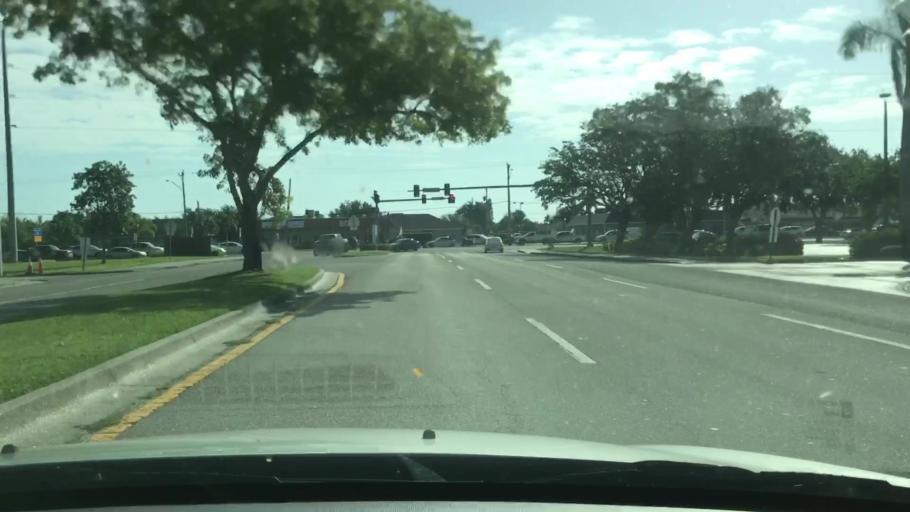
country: US
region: Florida
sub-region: Lee County
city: Lochmoor Waterway Estates
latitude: 26.6413
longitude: -81.9420
